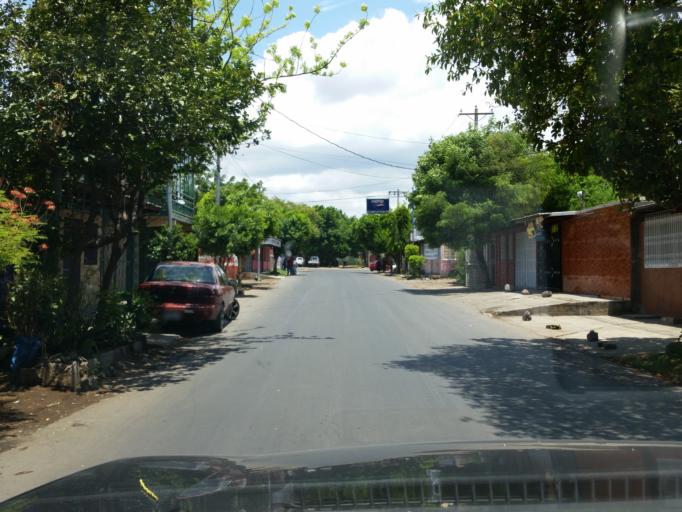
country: NI
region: Managua
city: Managua
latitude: 12.1429
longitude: -86.2188
